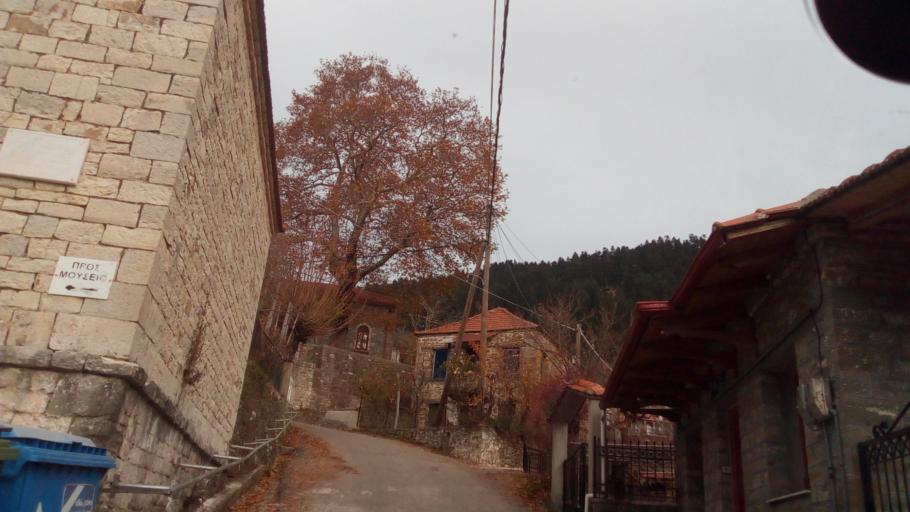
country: GR
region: West Greece
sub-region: Nomos Aitolias kai Akarnanias
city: Thermo
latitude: 38.6856
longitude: 21.8659
